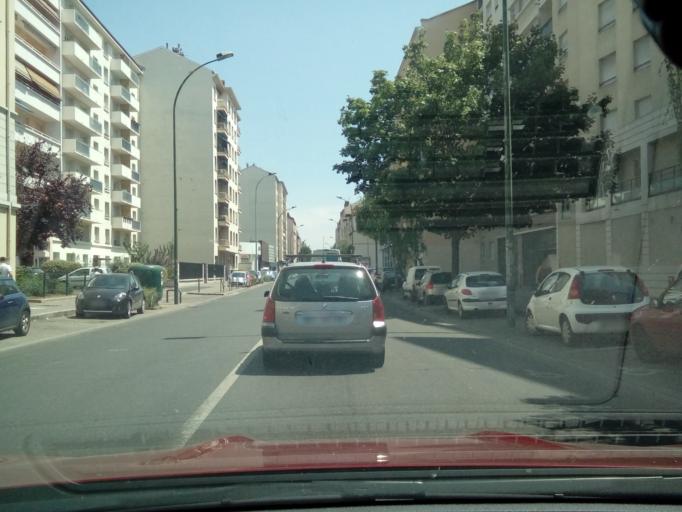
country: FR
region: Rhone-Alpes
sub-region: Departement du Rhone
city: Villeurbanne
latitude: 45.7675
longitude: 4.8907
